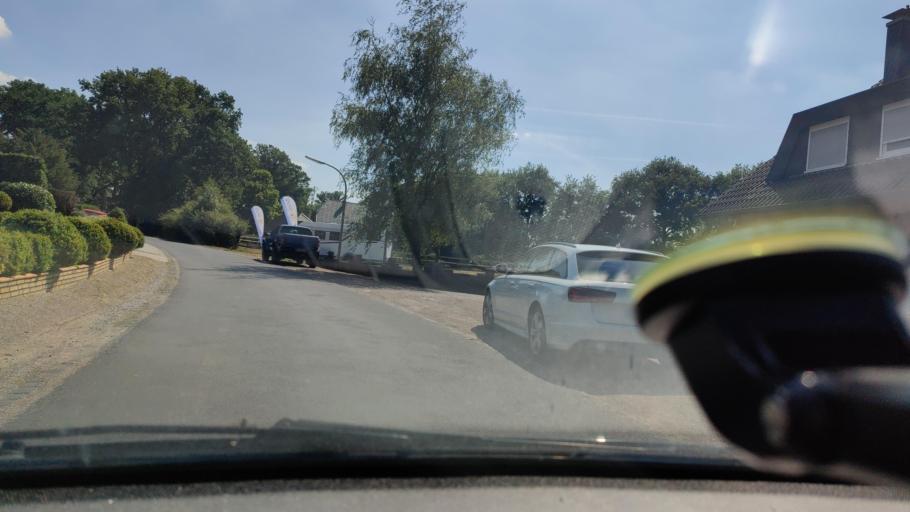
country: DE
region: North Rhine-Westphalia
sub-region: Regierungsbezirk Dusseldorf
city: Schermbeck
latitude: 51.6546
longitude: 6.9040
